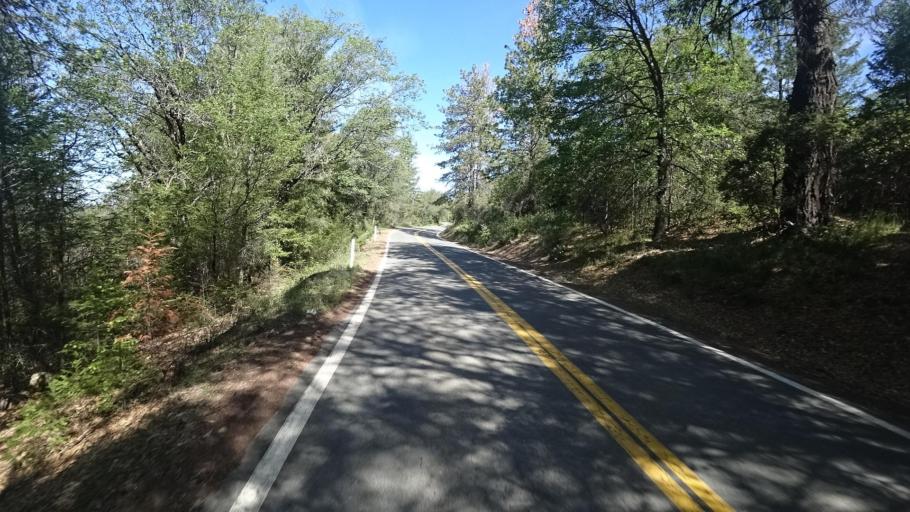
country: US
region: California
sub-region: Lake County
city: Cobb
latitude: 38.8818
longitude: -122.7827
